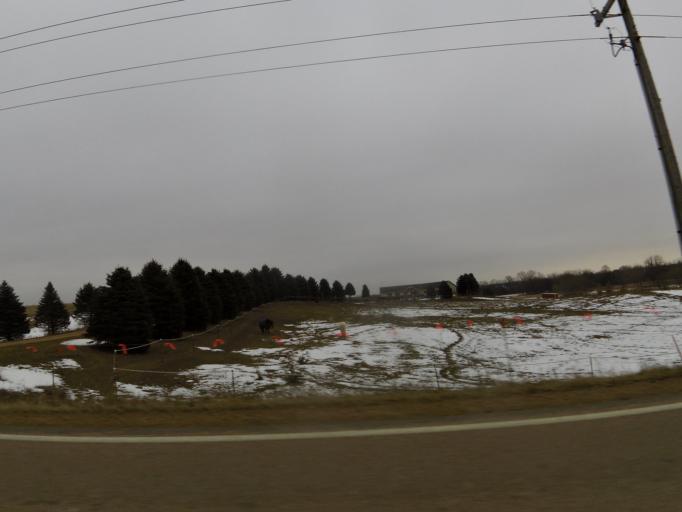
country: US
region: Minnesota
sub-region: Carver County
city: Carver
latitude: 44.7555
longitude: -93.6839
